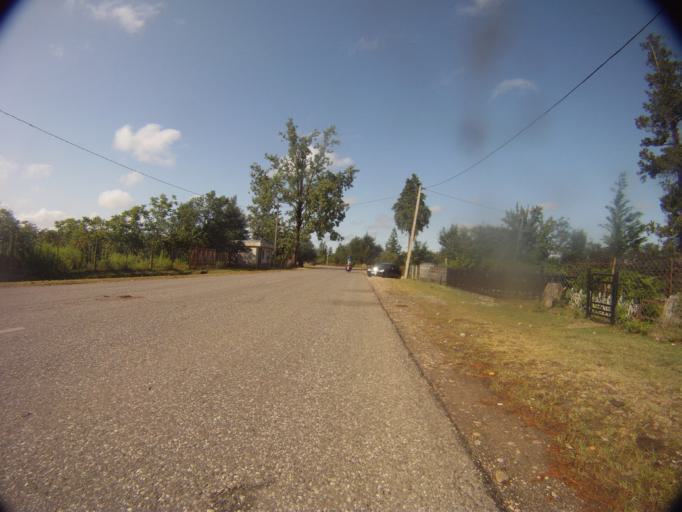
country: GE
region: Samegrelo and Zemo Svaneti
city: Kveda Chkhorots'q'u
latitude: 42.4205
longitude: 42.0845
